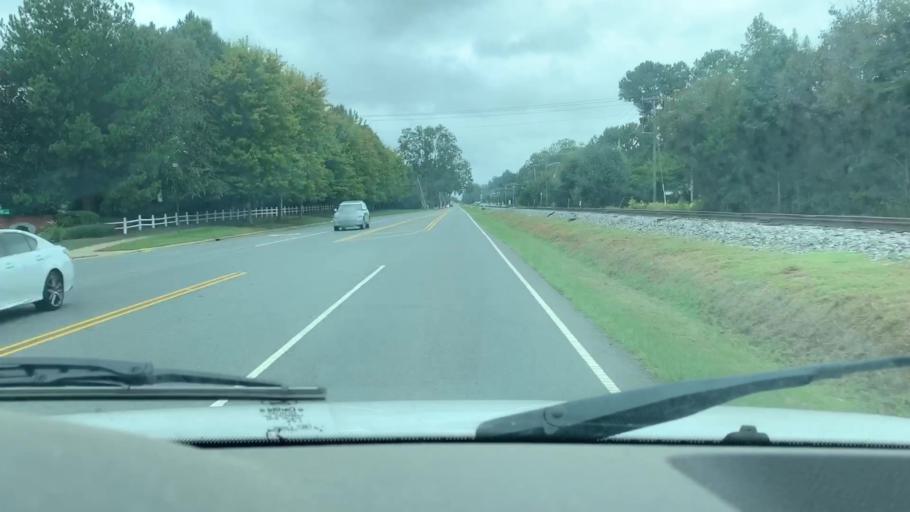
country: US
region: North Carolina
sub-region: Mecklenburg County
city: Cornelius
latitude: 35.4708
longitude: -80.8510
